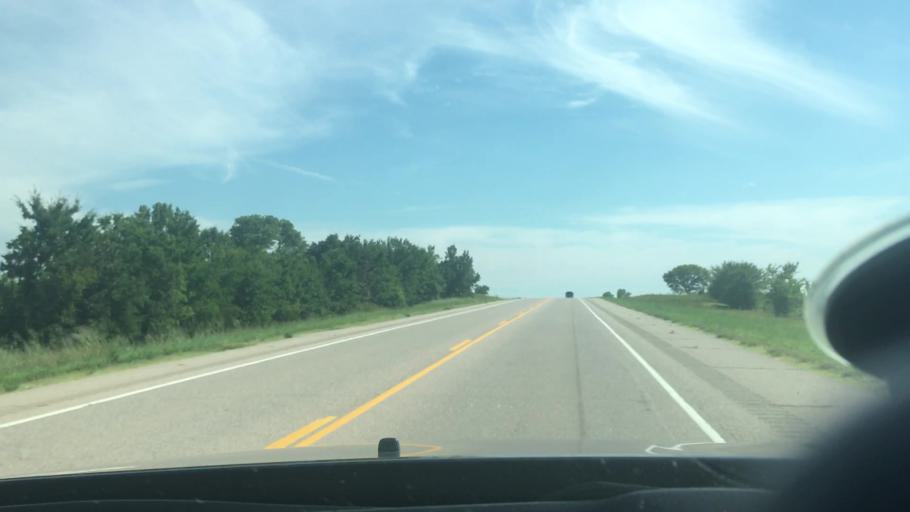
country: US
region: Oklahoma
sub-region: Seminole County
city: Maud
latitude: 35.0931
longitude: -96.6789
